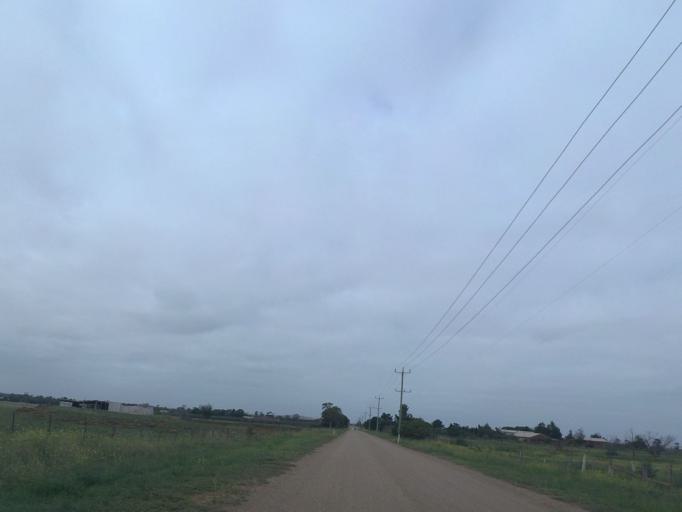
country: AU
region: Victoria
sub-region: Melton
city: Kurunjang
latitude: -37.6958
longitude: 144.6221
